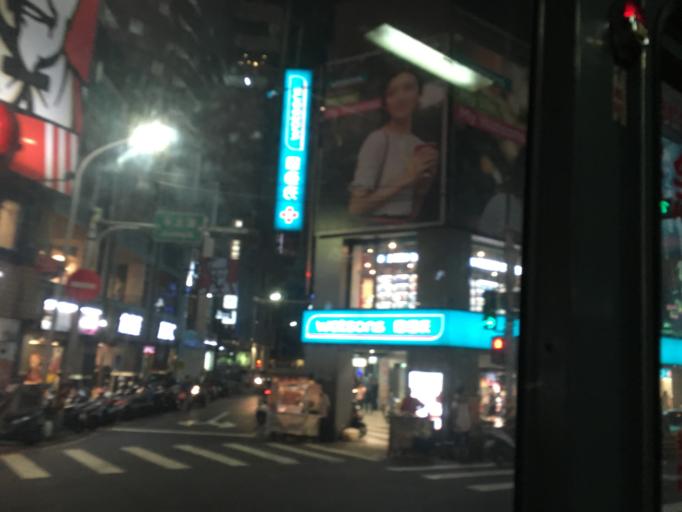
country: TW
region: Taiwan
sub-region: Hsinchu
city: Hsinchu
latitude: 24.8026
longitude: 120.9714
